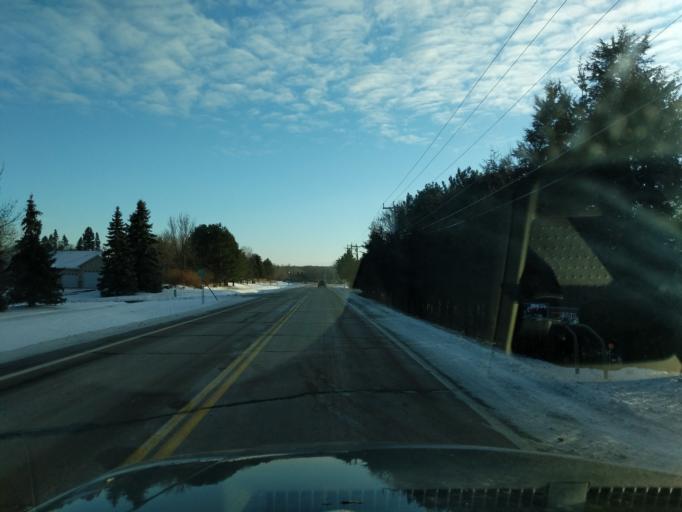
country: US
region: Minnesota
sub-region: Carver County
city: Victoria
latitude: 44.8781
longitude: -93.6414
